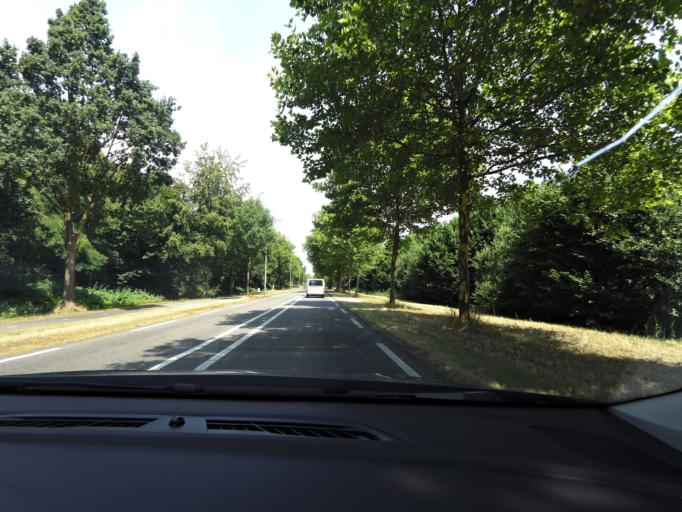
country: NL
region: Limburg
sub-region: Gemeente Weert
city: Weert
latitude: 51.2418
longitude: 5.7262
